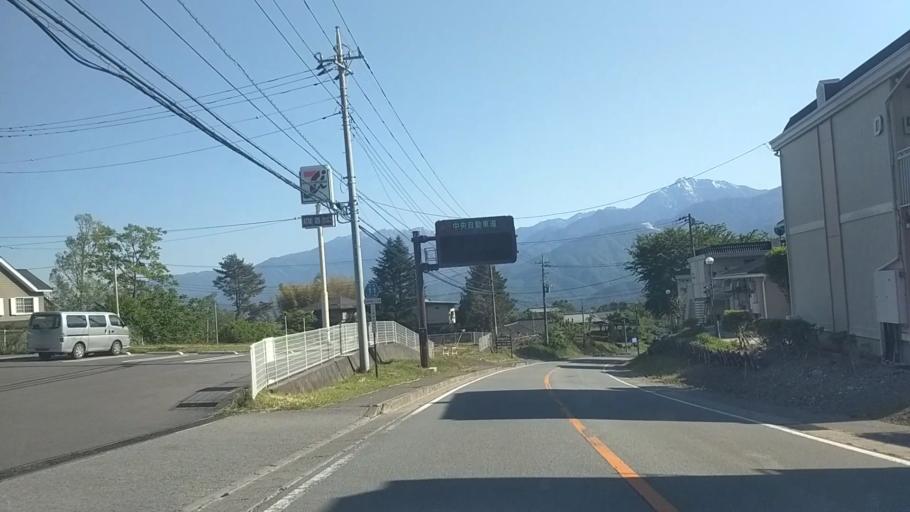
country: JP
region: Nagano
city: Chino
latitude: 35.8741
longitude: 138.3118
